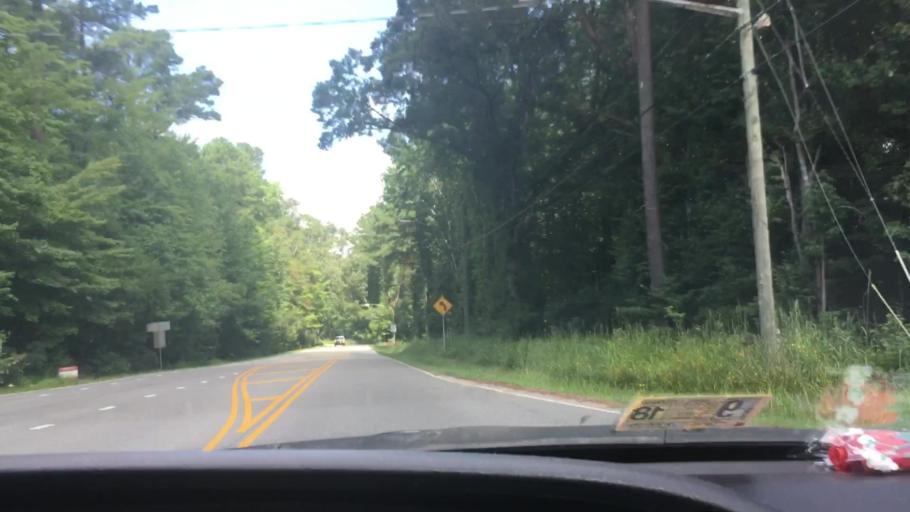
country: US
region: Virginia
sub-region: City of Virginia Beach
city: Virginia Beach
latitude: 36.7349
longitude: -76.0992
